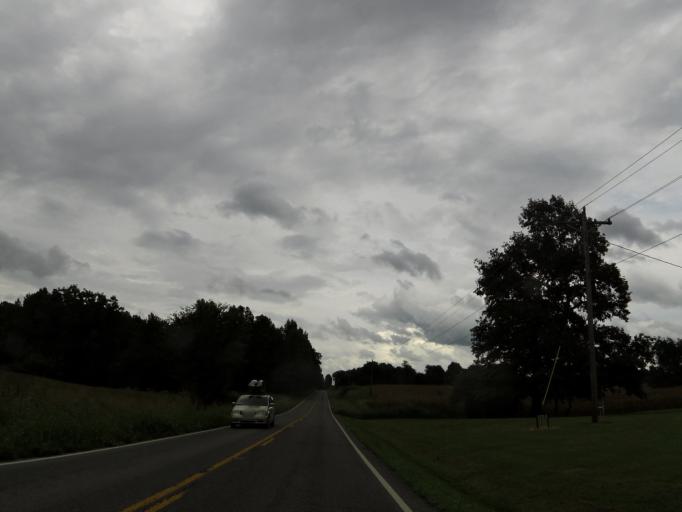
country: US
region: Kentucky
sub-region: Ballard County
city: Wickliffe
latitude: 36.9718
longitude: -89.0572
